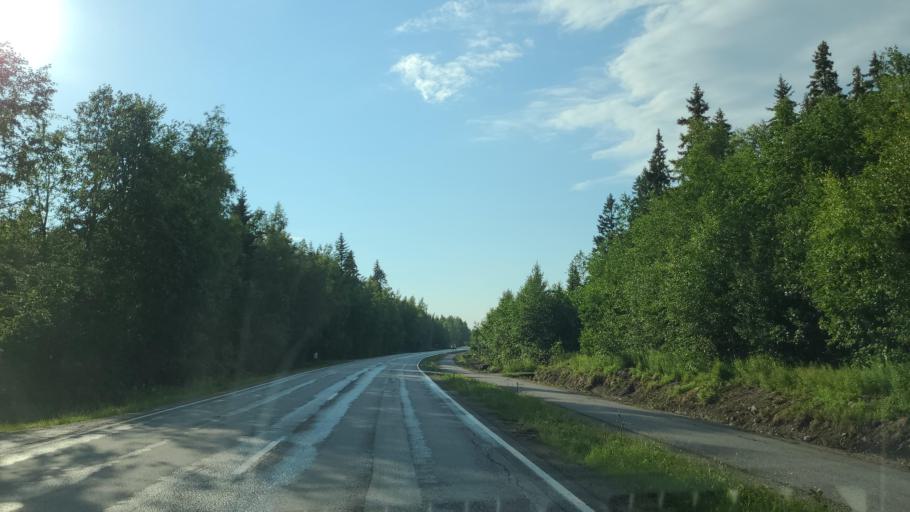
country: FI
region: Ostrobothnia
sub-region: Vaasa
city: Replot
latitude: 63.1991
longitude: 21.5369
